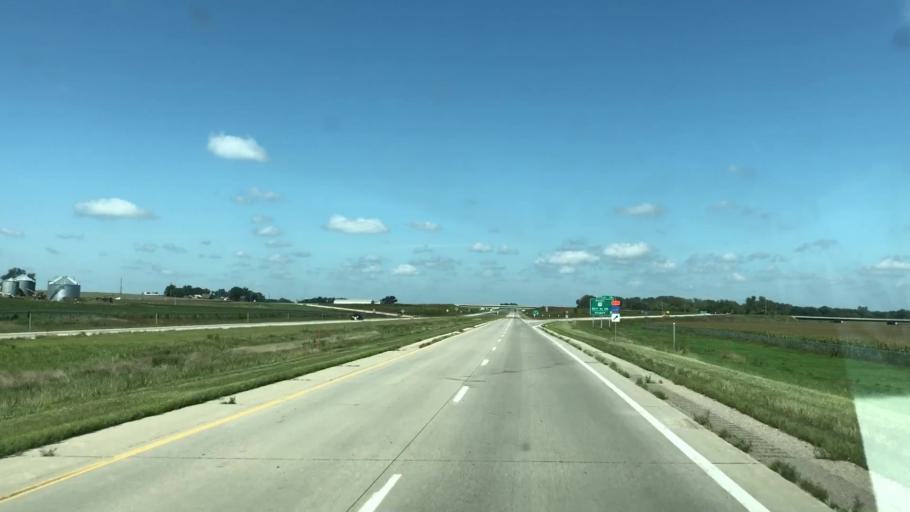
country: US
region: Iowa
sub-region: Plymouth County
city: Le Mars
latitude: 42.7572
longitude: -96.2091
